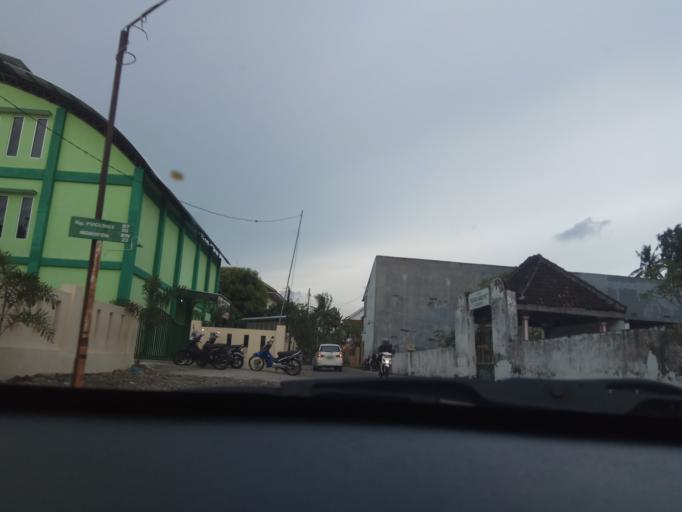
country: ID
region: Daerah Istimewa Yogyakarta
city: Depok
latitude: -7.7608
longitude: 110.4014
